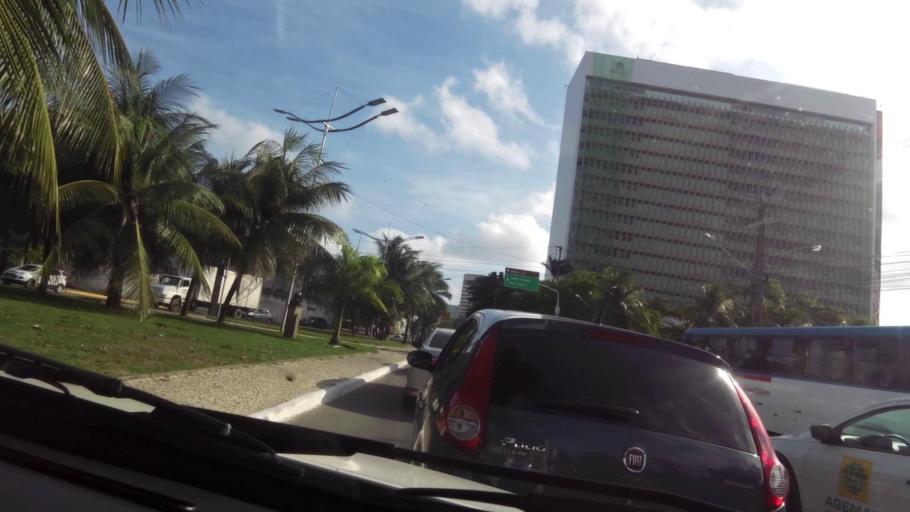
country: BR
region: Pernambuco
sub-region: Recife
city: Recife
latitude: -8.0539
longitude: -34.8719
